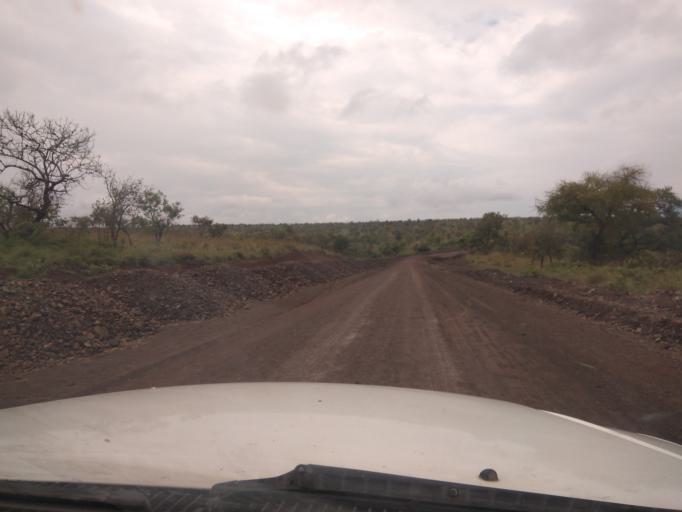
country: ET
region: Southern Nations, Nationalities, and People's Region
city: Felege Neway
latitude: 6.4305
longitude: 37.2640
